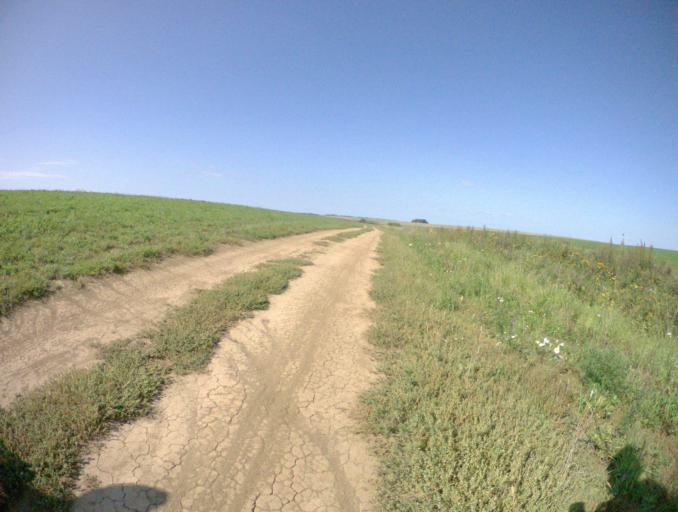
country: RU
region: Vladimir
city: Bogolyubovo
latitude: 56.2299
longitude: 40.4945
